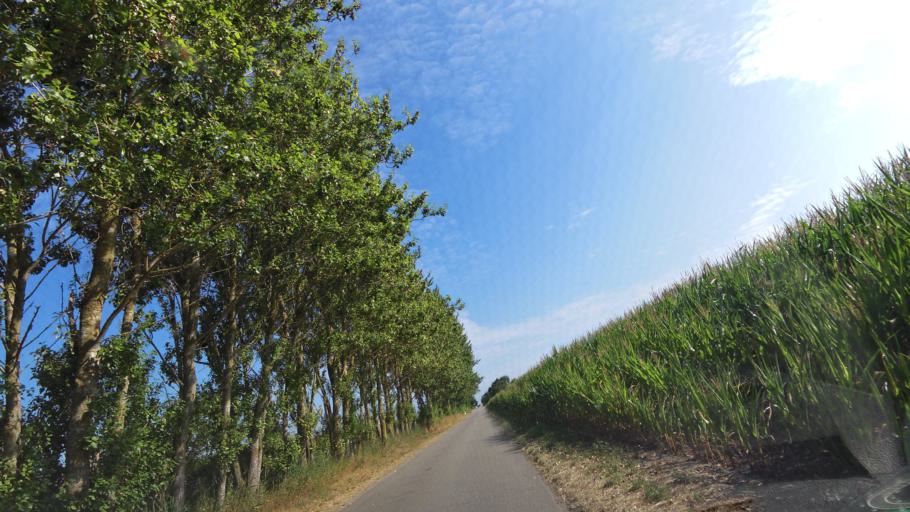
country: DK
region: South Denmark
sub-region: Nordfyns Kommune
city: Otterup
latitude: 55.5899
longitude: 10.3970
